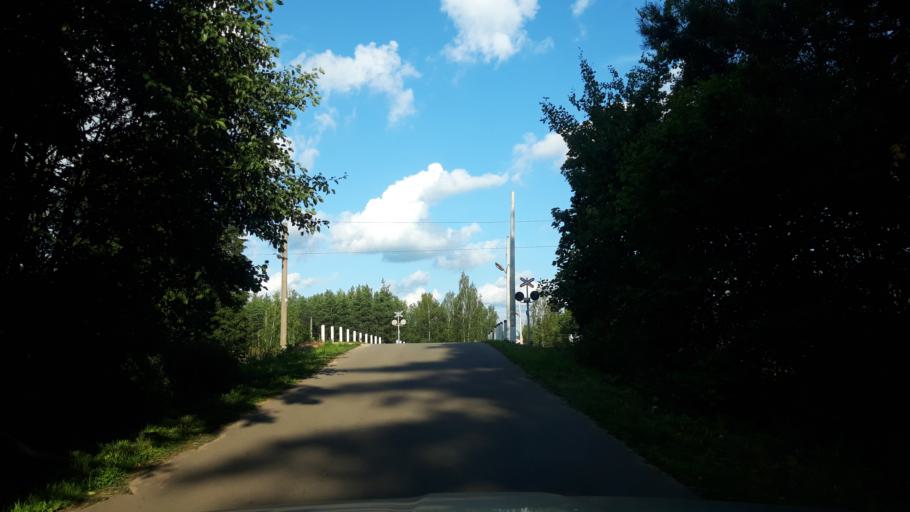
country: RU
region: Moskovskaya
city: Povarovo
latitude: 56.0622
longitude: 37.0832
